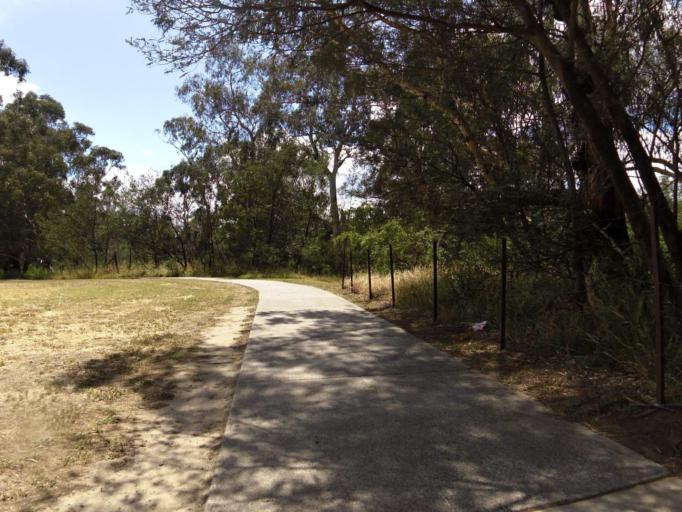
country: AU
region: Victoria
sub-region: Nillumbik
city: Eltham North
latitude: -37.6864
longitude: 145.1543
